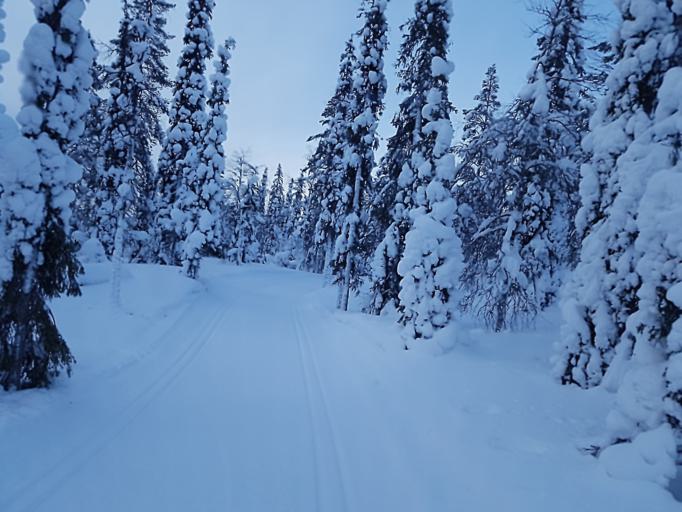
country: FI
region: Lapland
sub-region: Tunturi-Lappi
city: Kolari
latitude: 67.6532
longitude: 24.2469
